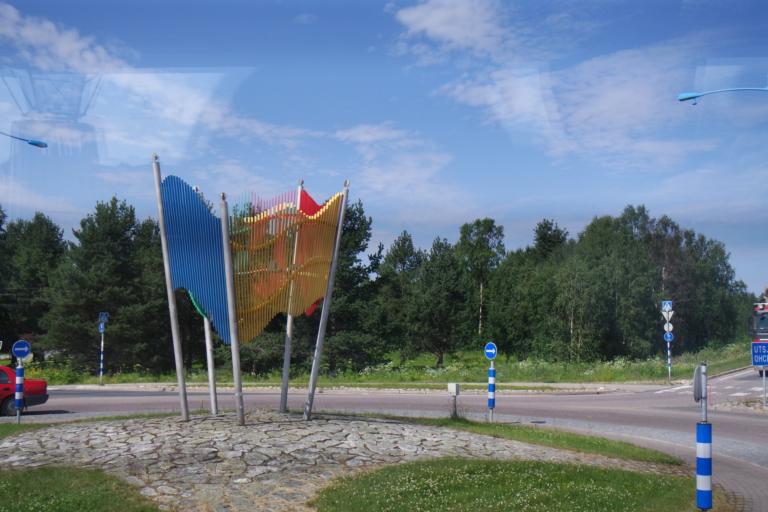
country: FI
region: Lapland
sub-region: Pohjois-Lappi
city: Ivalo
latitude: 68.6590
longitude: 27.5395
